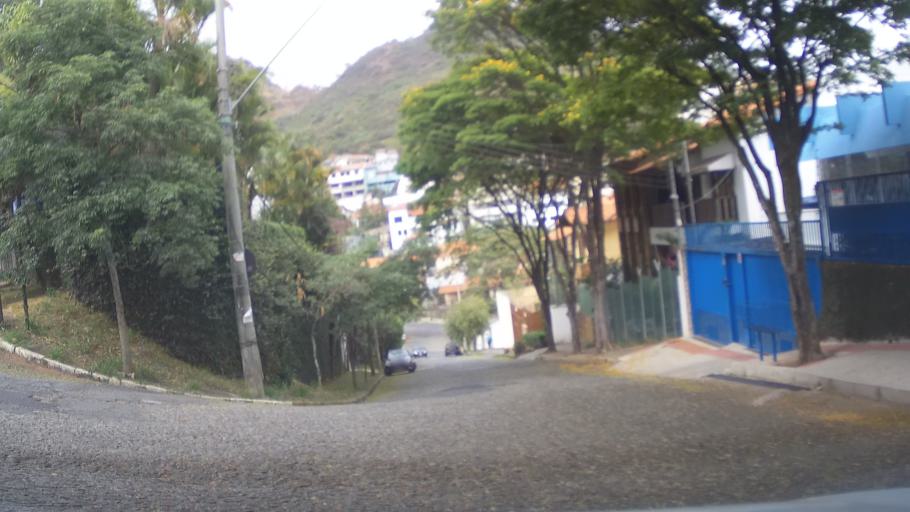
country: BR
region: Minas Gerais
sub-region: Belo Horizonte
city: Belo Horizonte
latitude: -19.9530
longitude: -43.9202
